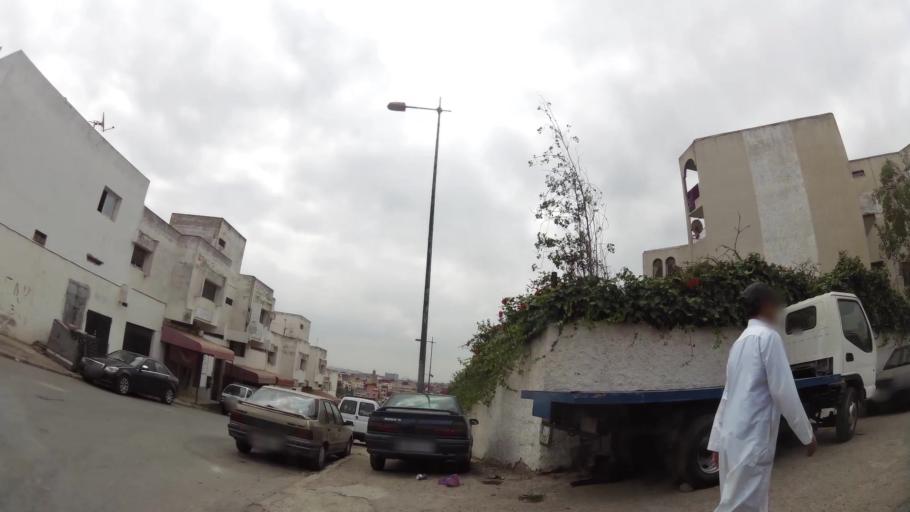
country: MA
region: Rabat-Sale-Zemmour-Zaer
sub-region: Rabat
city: Rabat
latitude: 33.9953
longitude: -6.8730
